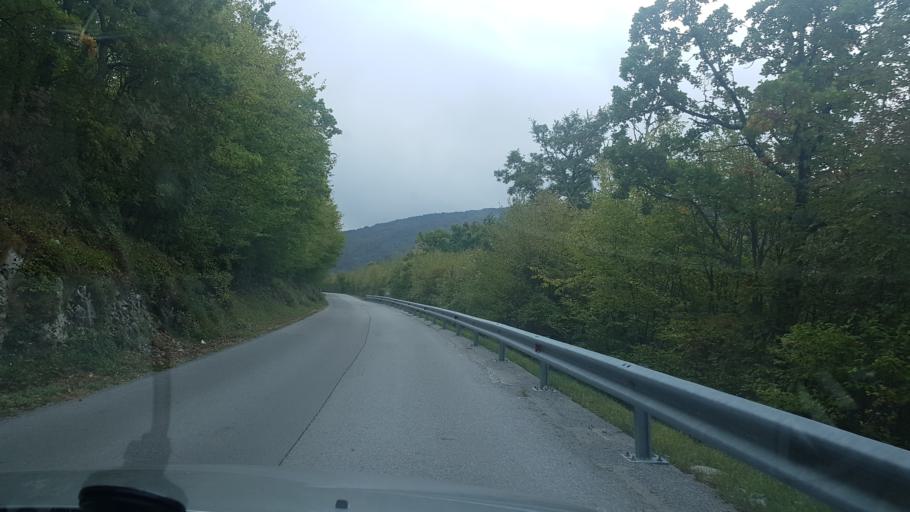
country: SI
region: Hrpelje-Kozina
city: Kozina
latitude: 45.5204
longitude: 13.9565
